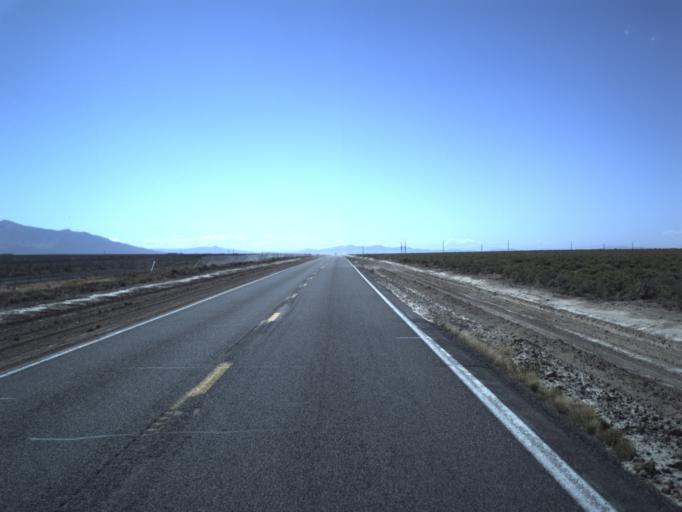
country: US
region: Utah
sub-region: Beaver County
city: Milford
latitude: 38.5129
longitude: -112.9912
